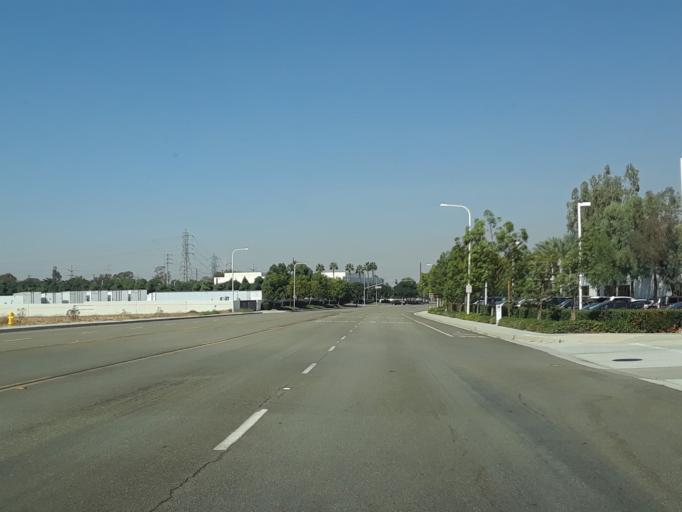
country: US
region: California
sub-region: Orange County
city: Irvine
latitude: 33.6629
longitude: -117.7612
